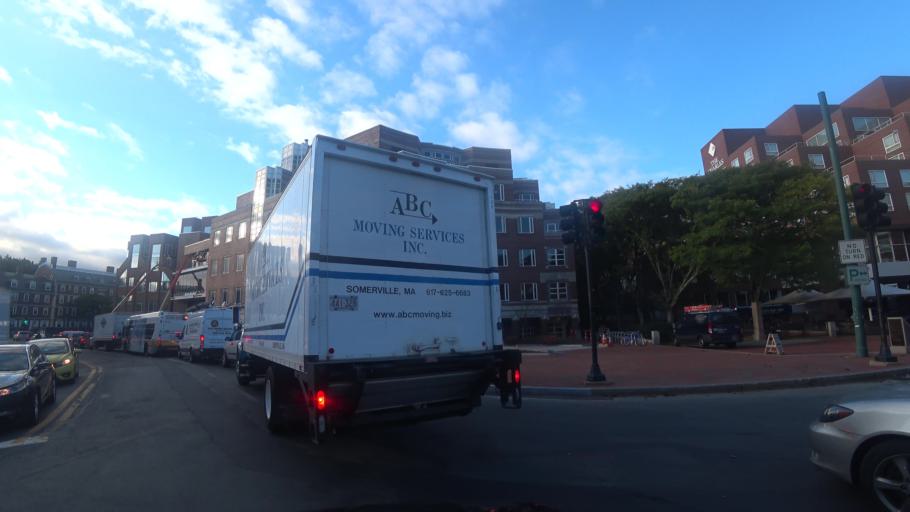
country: US
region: Massachusetts
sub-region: Middlesex County
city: Cambridge
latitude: 42.3724
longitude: -71.1218
